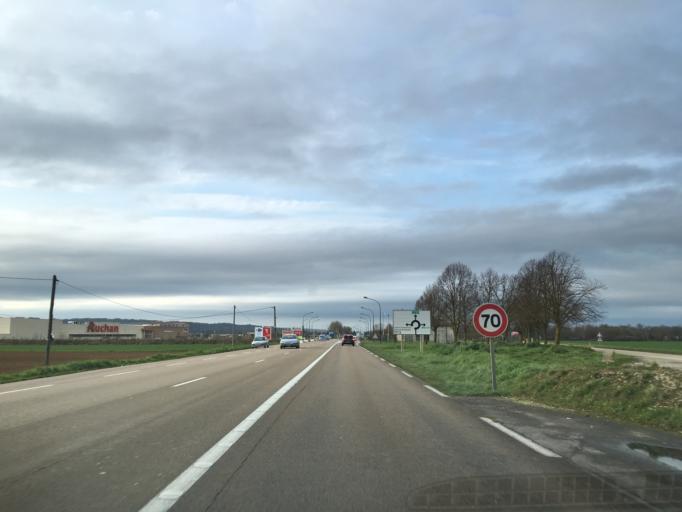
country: FR
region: Bourgogne
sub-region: Departement de l'Yonne
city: Maillot
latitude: 48.1698
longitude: 3.2968
